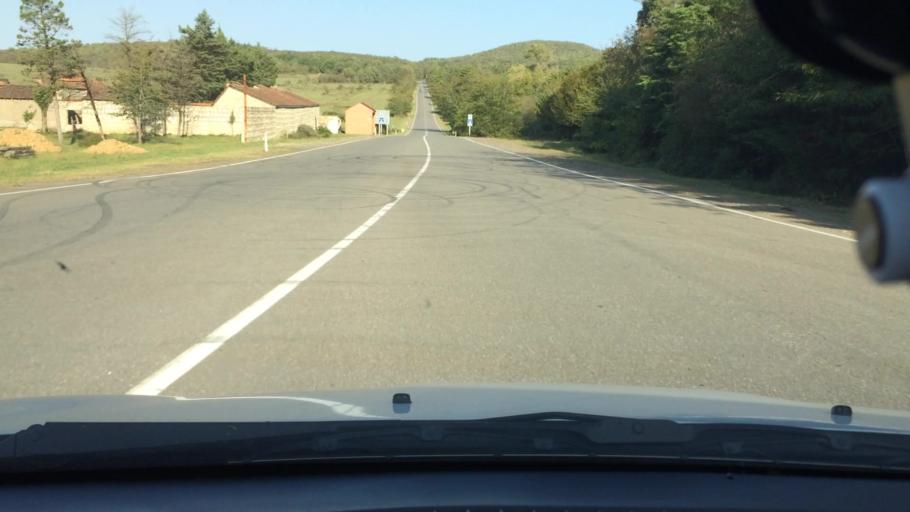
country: GE
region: Imereti
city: Kutaisi
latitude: 42.2402
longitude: 42.7656
